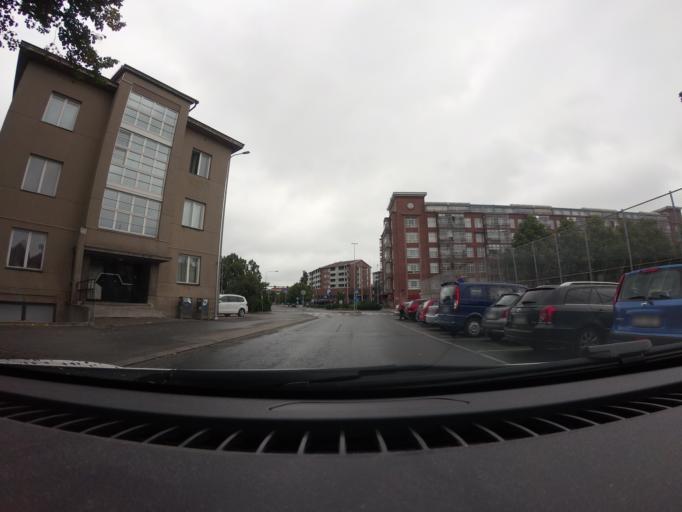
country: FI
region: Varsinais-Suomi
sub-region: Turku
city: Turku
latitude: 60.4573
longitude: 22.2719
